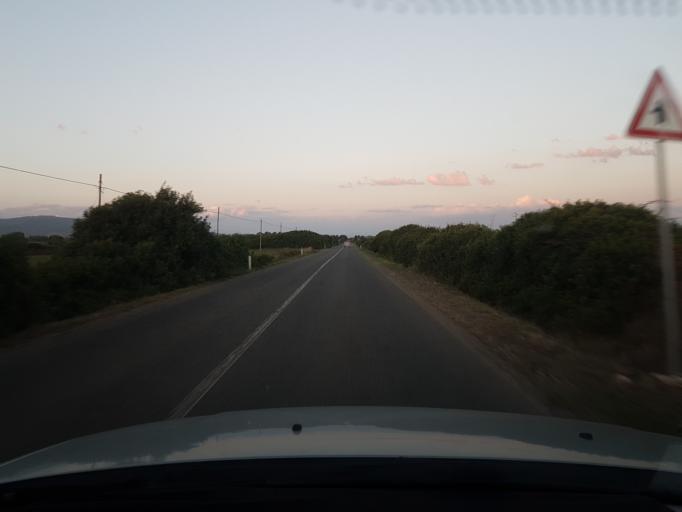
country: IT
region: Sardinia
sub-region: Provincia di Oristano
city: Riola Sardo
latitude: 40.0219
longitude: 8.4638
